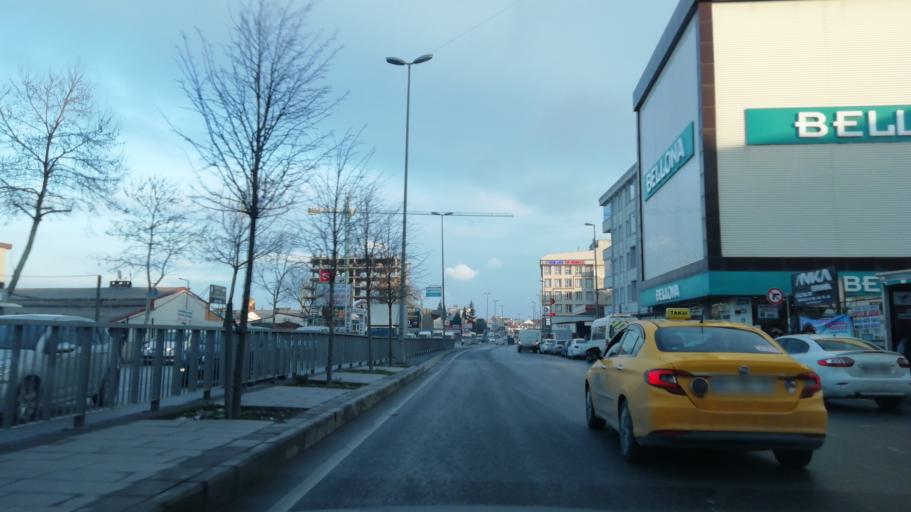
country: TR
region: Istanbul
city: Esenyurt
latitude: 41.0123
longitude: 28.6972
